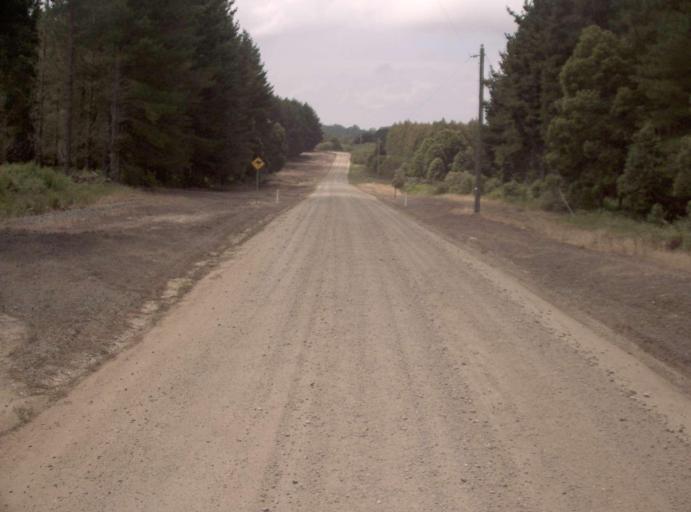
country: AU
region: Victoria
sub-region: Latrobe
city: Traralgon
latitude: -38.3968
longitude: 146.6575
